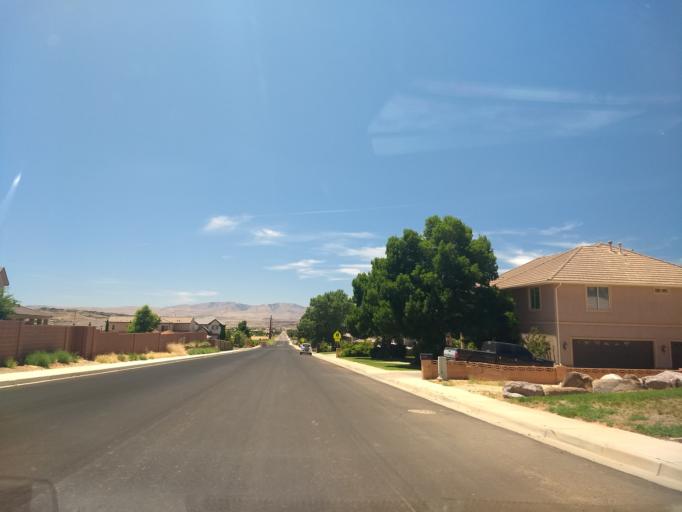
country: US
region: Utah
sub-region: Washington County
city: Washington
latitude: 37.0890
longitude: -113.4937
